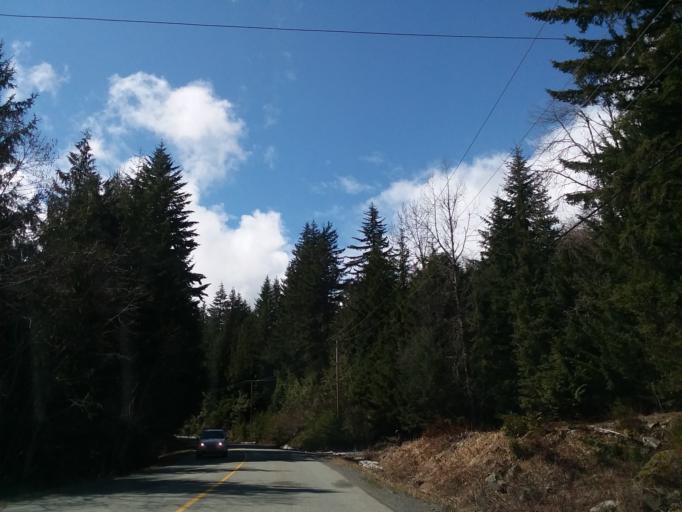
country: CA
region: British Columbia
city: Whistler
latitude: 50.1102
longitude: -122.9880
